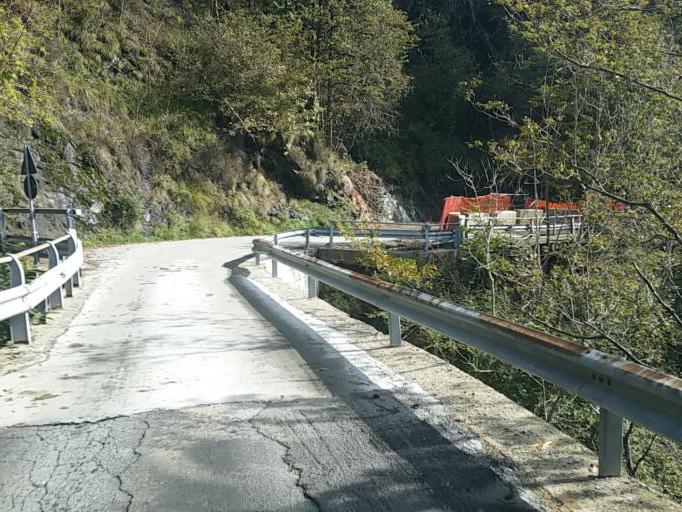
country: IT
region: Piedmont
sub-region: Provincia Verbano-Cusio-Ossola
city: Cursolo
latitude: 46.0975
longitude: 8.5570
